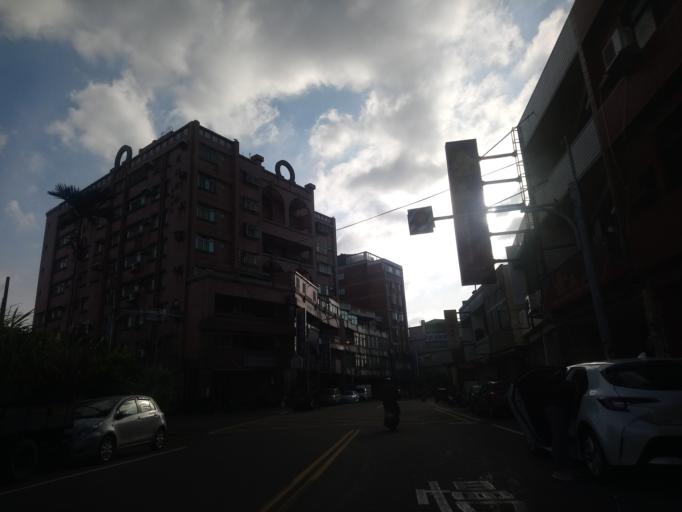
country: TW
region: Taiwan
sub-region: Hsinchu
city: Hsinchu
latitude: 24.7986
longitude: 120.9447
